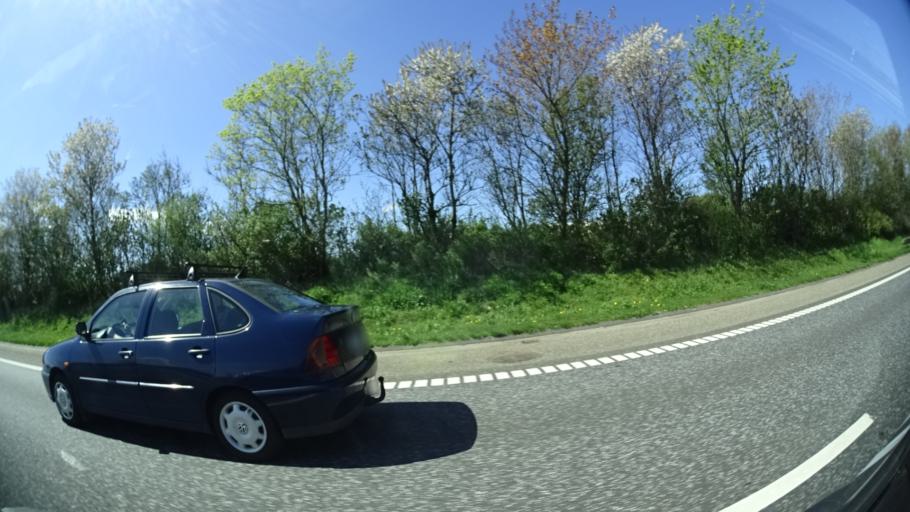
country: DK
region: Central Jutland
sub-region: Arhus Kommune
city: Trige
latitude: 56.2787
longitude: 10.1357
